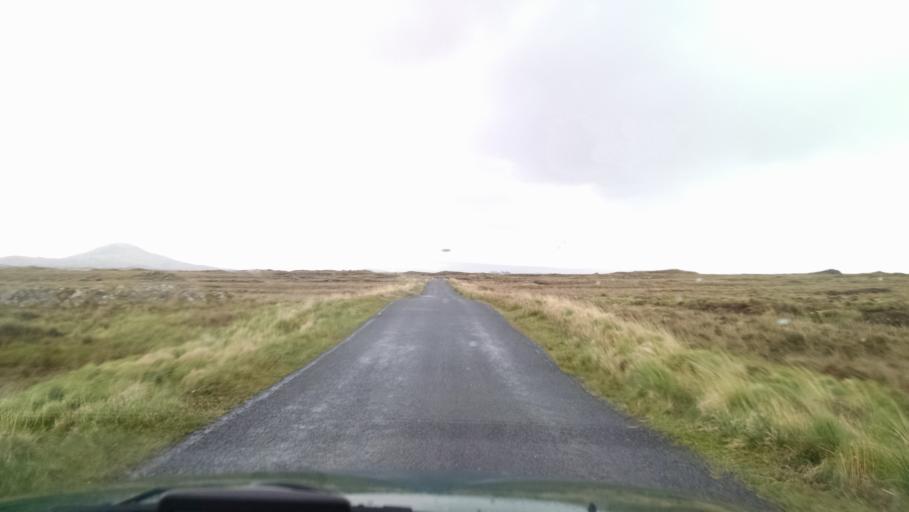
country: IE
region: Connaught
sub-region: County Galway
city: Clifden
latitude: 53.4388
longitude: -9.9184
